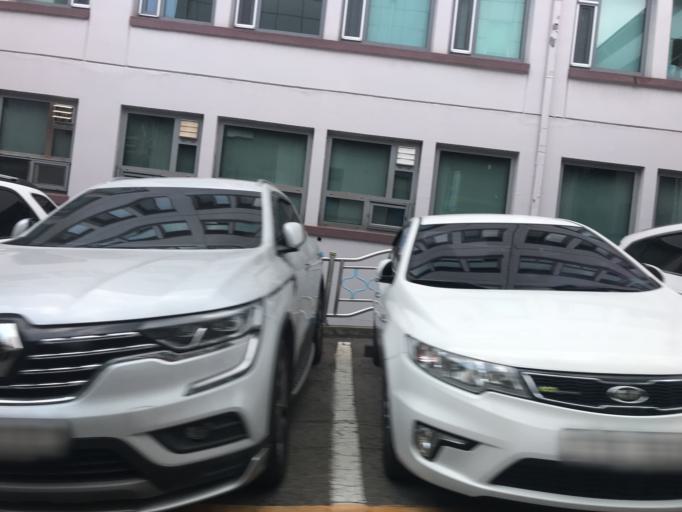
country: KR
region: Seoul
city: Seoul
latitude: 37.5623
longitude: 126.9393
